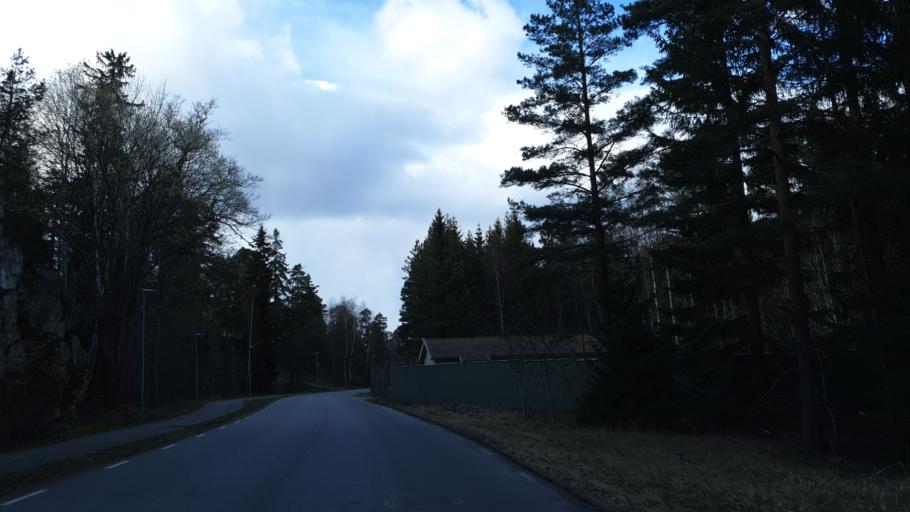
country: SE
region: Stockholm
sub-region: Lidingo
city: Lidingoe
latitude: 59.3847
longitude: 18.1187
